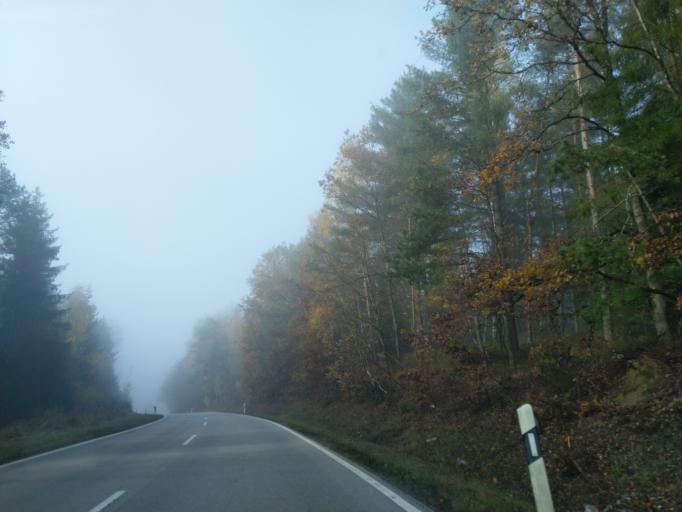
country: DE
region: Bavaria
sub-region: Lower Bavaria
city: Aussernzell
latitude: 48.7242
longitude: 13.2214
